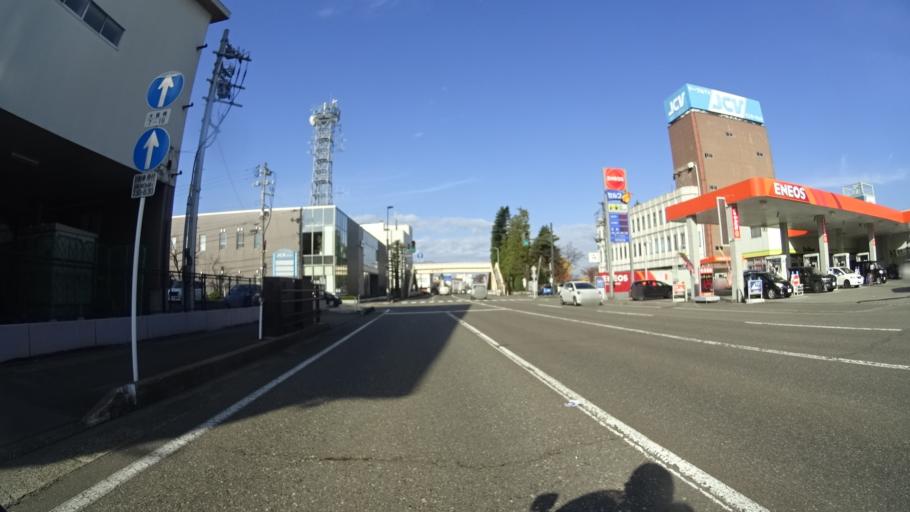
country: JP
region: Niigata
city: Joetsu
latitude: 37.1124
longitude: 138.2507
